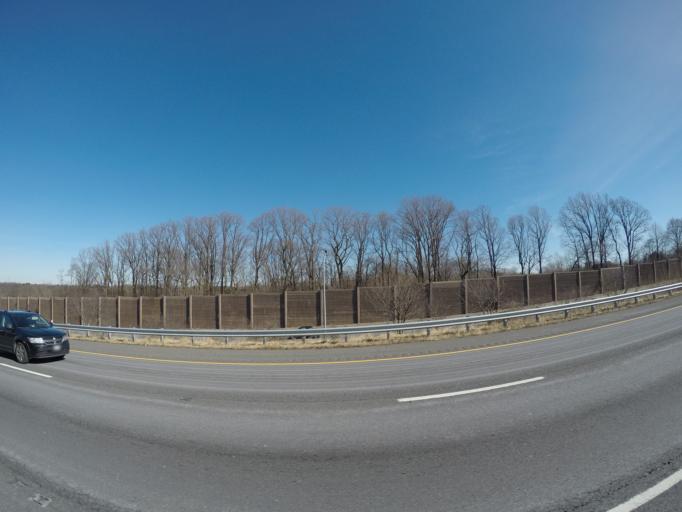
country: US
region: Maryland
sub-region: Howard County
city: Columbia
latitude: 39.2339
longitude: -76.8139
